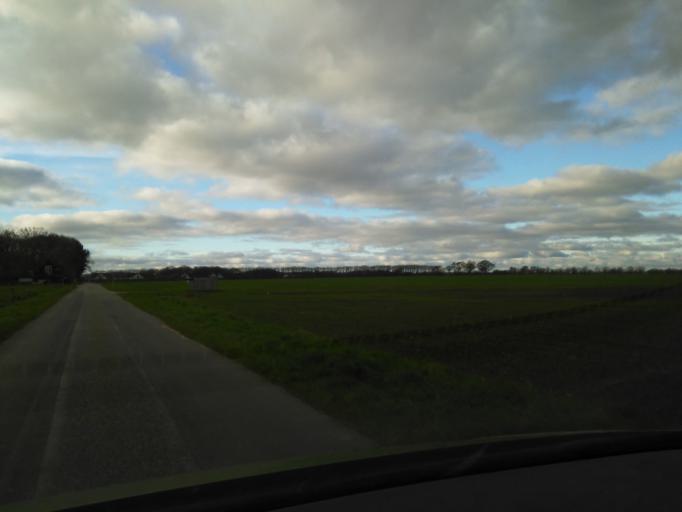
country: DK
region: Central Jutland
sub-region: Odder Kommune
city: Odder
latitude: 55.8722
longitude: 10.1785
